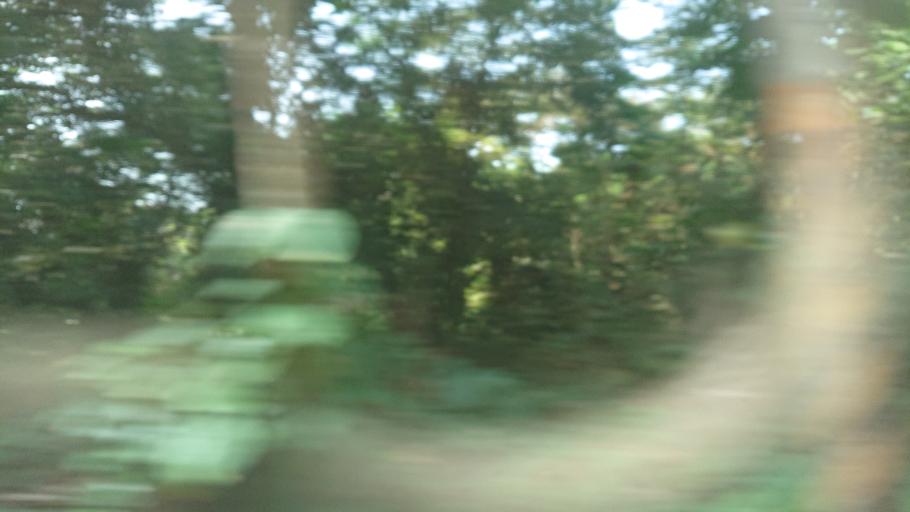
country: TW
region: Taiwan
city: Lugu
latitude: 23.7230
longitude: 120.6685
